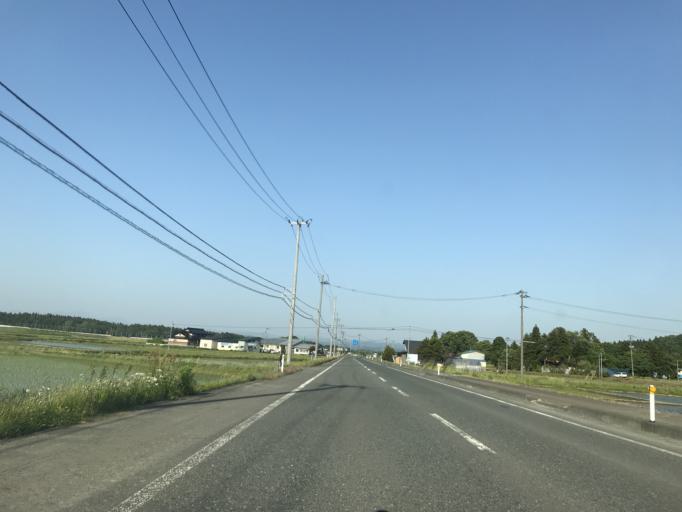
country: JP
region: Iwate
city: Kitakami
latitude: 39.2832
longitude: 141.0277
